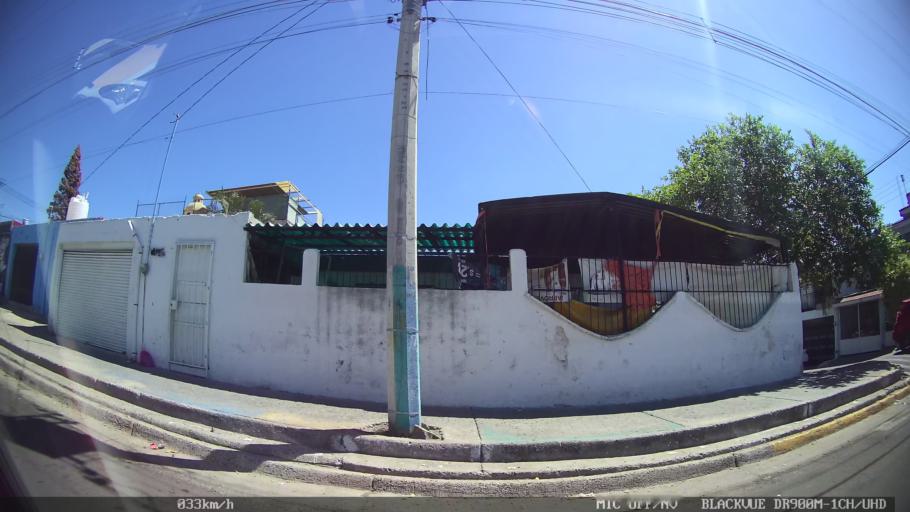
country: MX
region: Jalisco
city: Tlaquepaque
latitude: 20.6933
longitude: -103.2873
